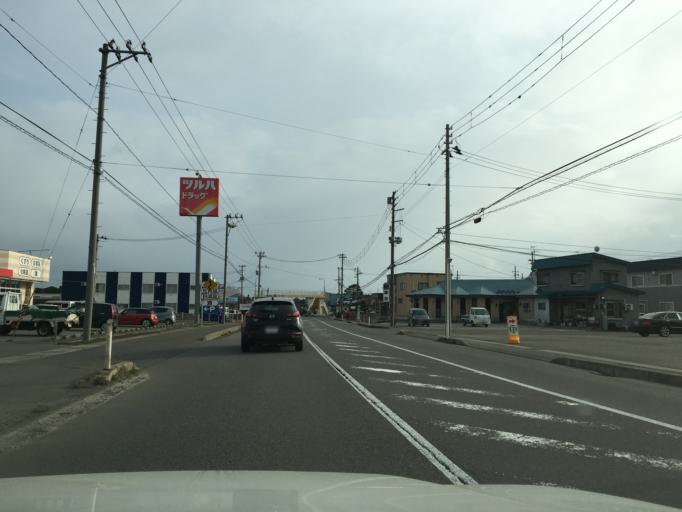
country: JP
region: Aomori
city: Namioka
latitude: 40.7210
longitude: 140.5889
